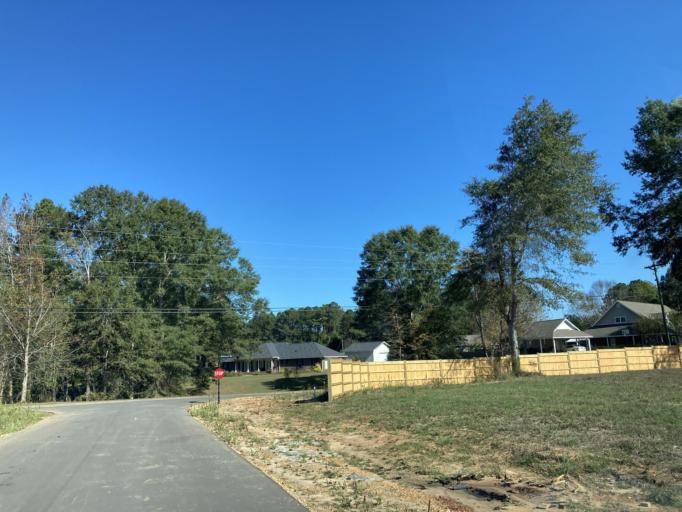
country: US
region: Mississippi
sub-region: Lamar County
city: West Hattiesburg
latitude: 31.2989
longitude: -89.4178
